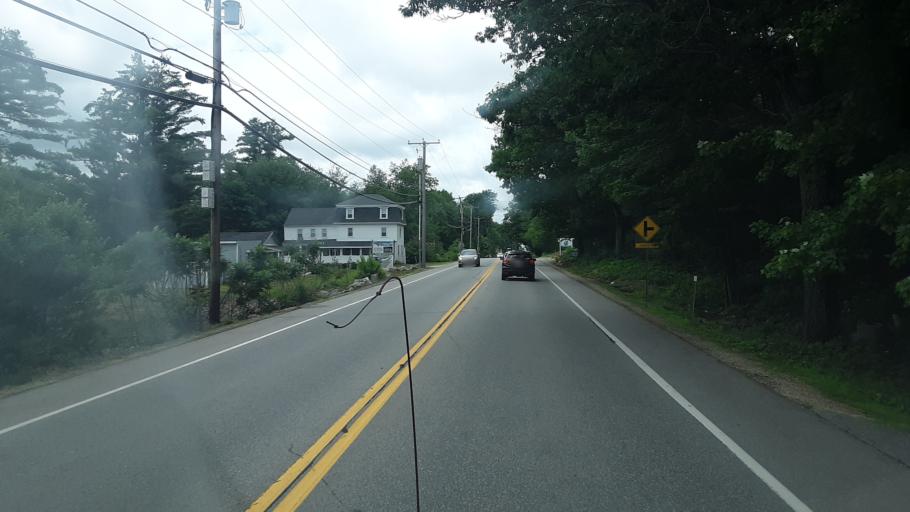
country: US
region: New Hampshire
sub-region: Rockingham County
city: Northwood
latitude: 43.2199
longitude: -71.2160
